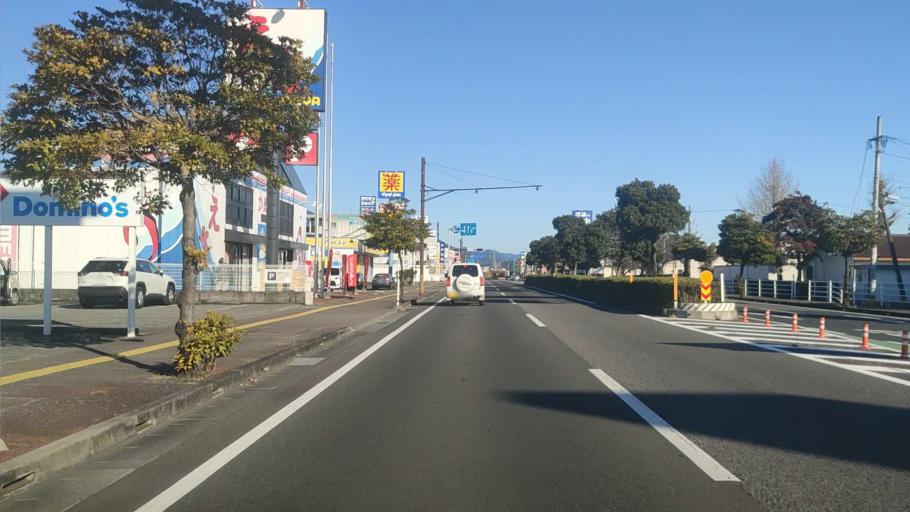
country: JP
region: Miyazaki
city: Nobeoka
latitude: 32.5726
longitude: 131.6836
